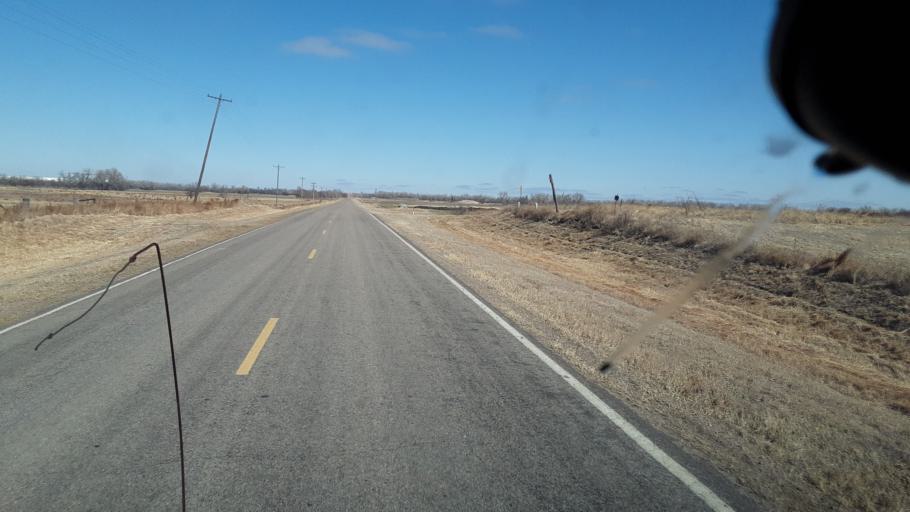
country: US
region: Kansas
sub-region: Barton County
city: Ellinwood
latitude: 38.3402
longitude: -98.6642
